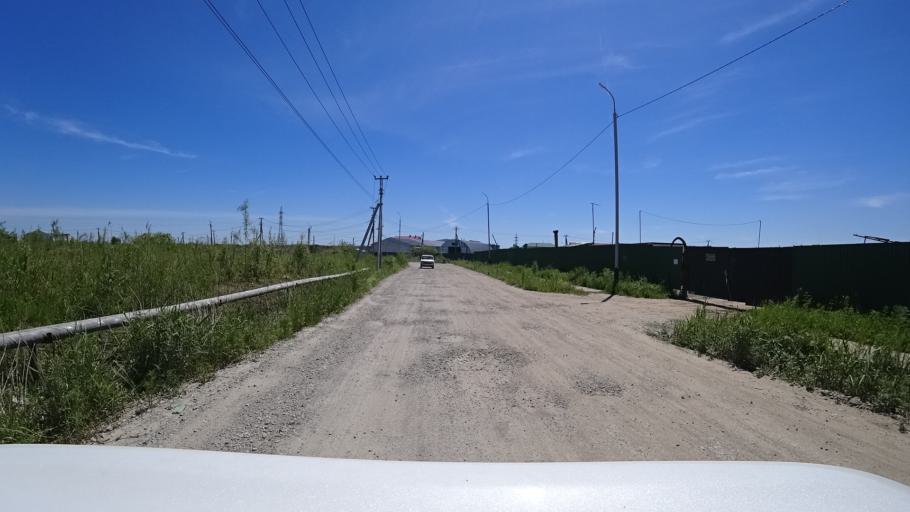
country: RU
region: Khabarovsk Krai
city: Topolevo
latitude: 48.5028
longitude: 135.1823
